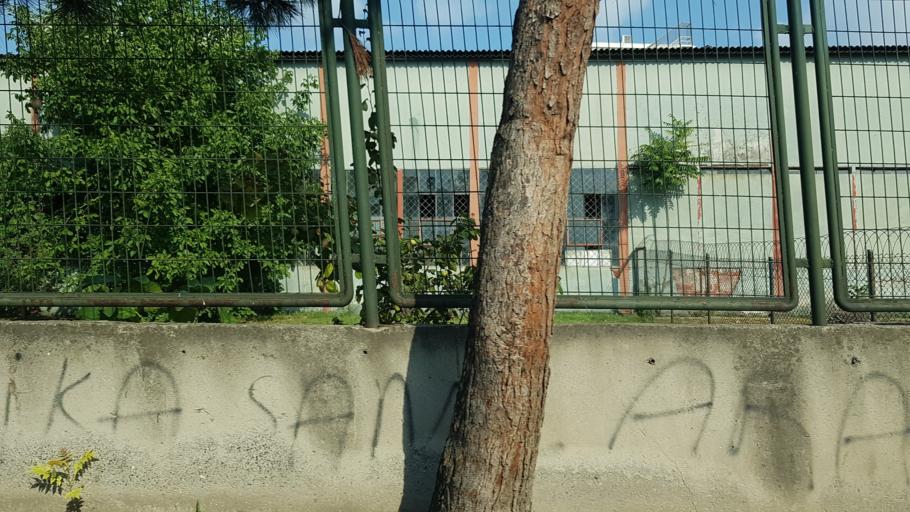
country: TR
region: Istanbul
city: Maltepe
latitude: 40.9049
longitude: 29.1967
